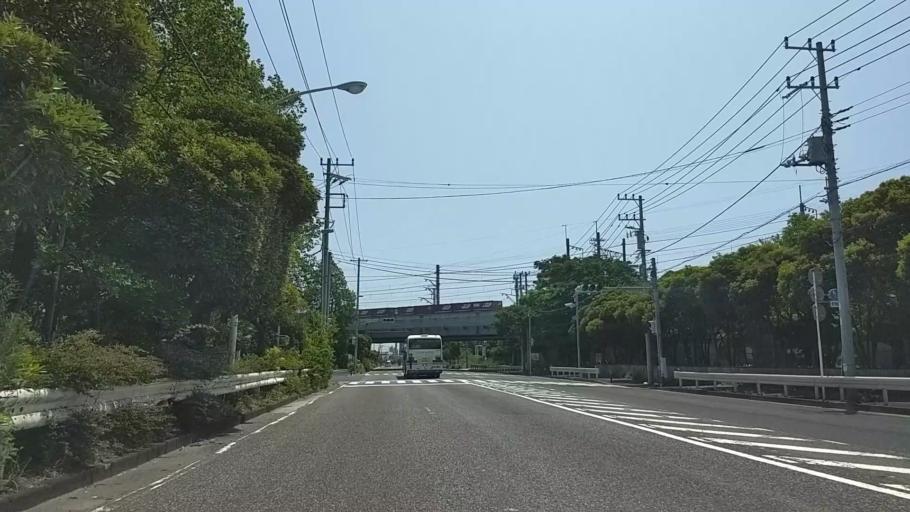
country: JP
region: Kanagawa
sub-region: Kawasaki-shi
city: Kawasaki
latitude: 35.5210
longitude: 139.7323
